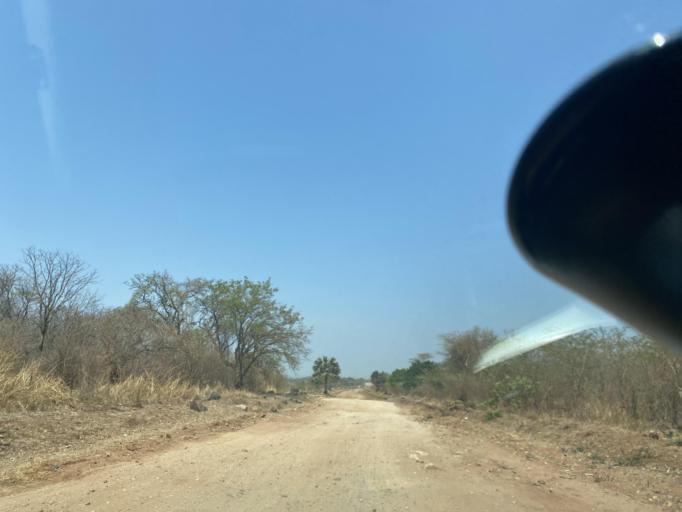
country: ZM
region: Lusaka
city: Lusaka
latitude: -15.5310
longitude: 28.0965
